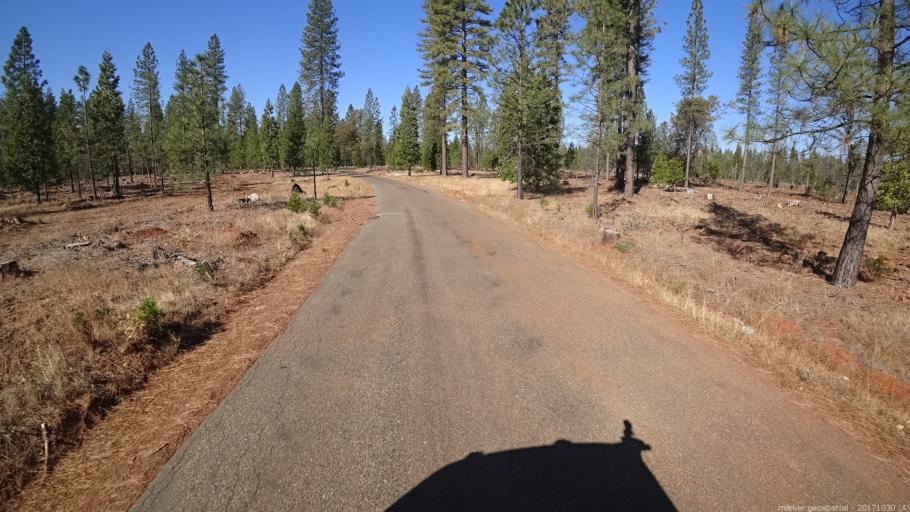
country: US
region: California
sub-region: Shasta County
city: Shingletown
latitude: 40.6094
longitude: -121.8635
